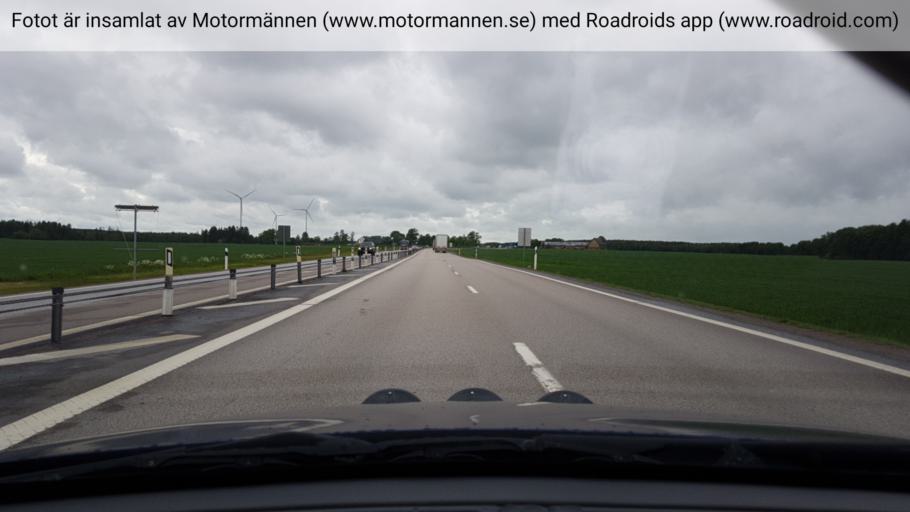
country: SE
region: Vaestra Goetaland
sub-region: Skara Kommun
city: Skara
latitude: 58.3750
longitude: 13.4016
